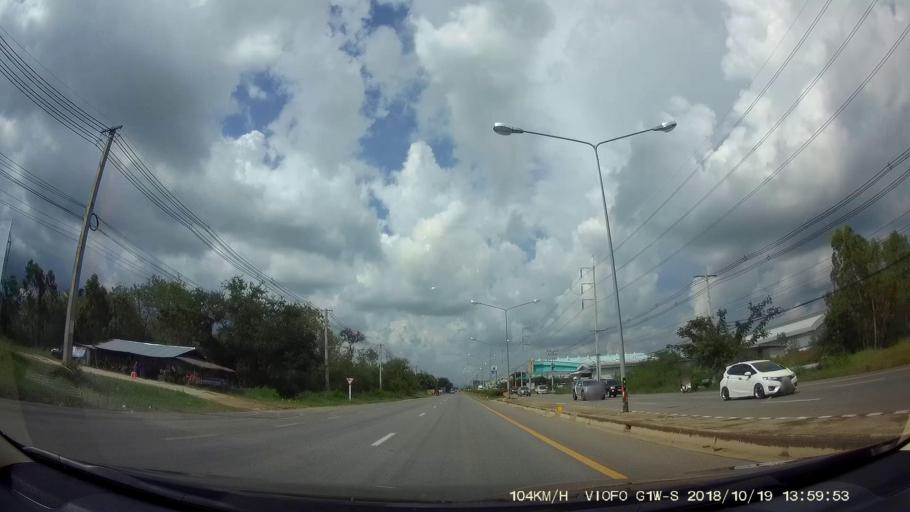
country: TH
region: Chaiyaphum
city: Chaiyaphum
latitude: 15.8164
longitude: 102.0601
